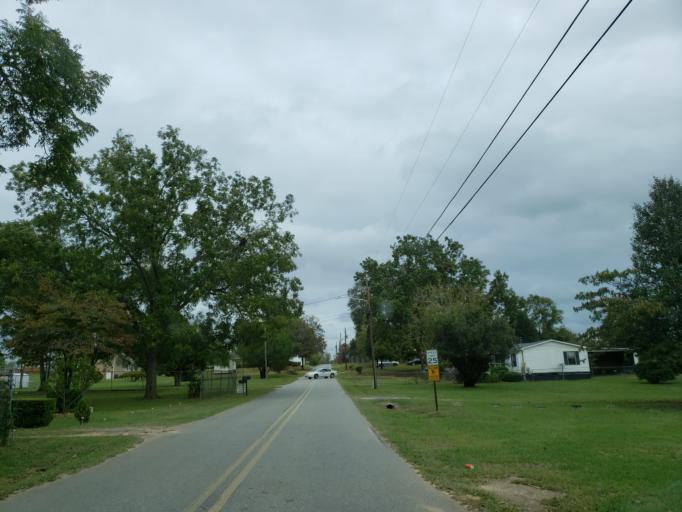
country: US
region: Georgia
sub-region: Dooly County
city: Vienna
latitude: 32.0904
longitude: -83.7820
